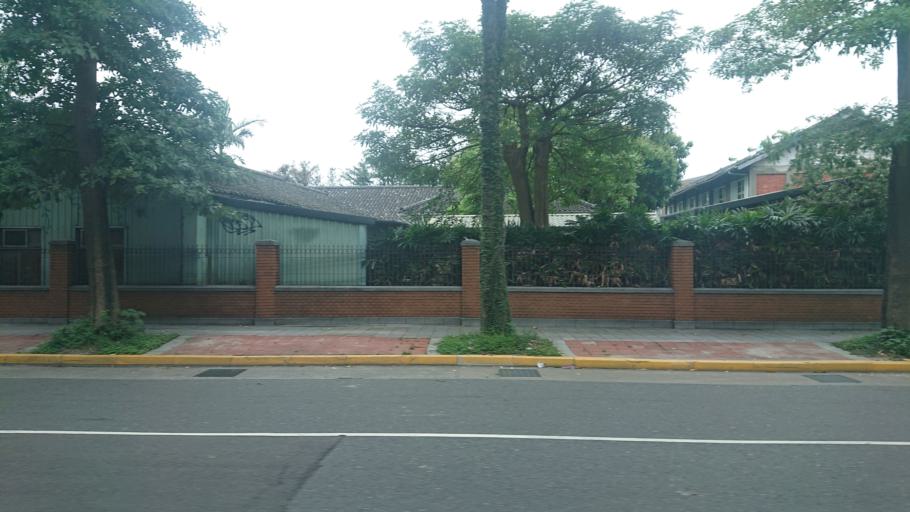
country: TW
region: Taipei
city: Taipei
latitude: 25.0154
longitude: 121.5417
